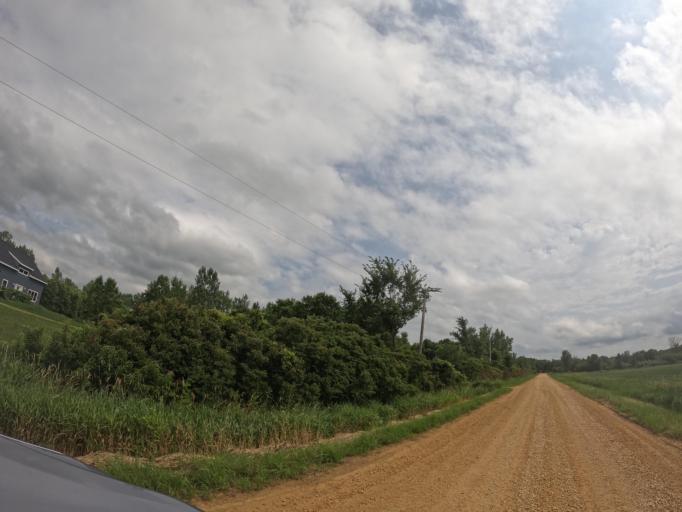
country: US
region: Iowa
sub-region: Clinton County
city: De Witt
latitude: 41.7753
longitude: -90.5828
